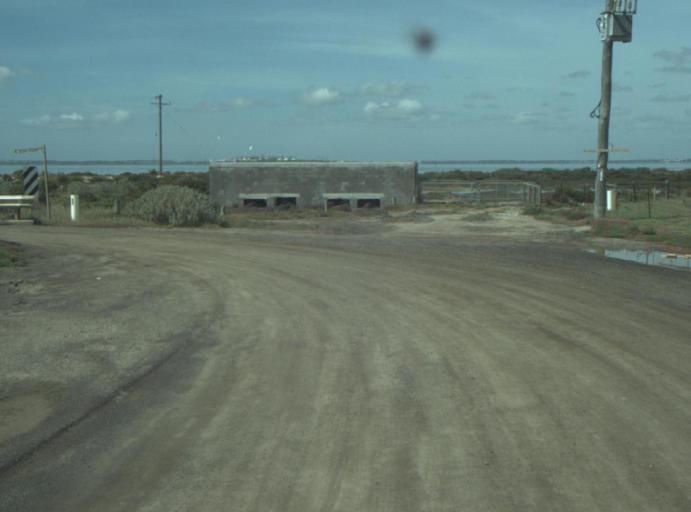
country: AU
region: Victoria
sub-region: Greater Geelong
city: Lara
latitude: -38.0835
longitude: 144.4225
